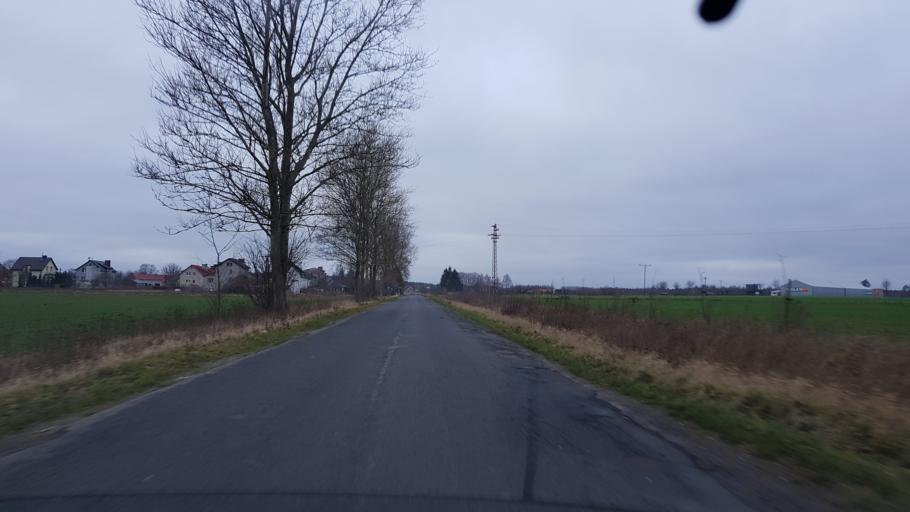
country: PL
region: West Pomeranian Voivodeship
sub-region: Powiat slawienski
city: Slawno
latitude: 54.3678
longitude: 16.7299
